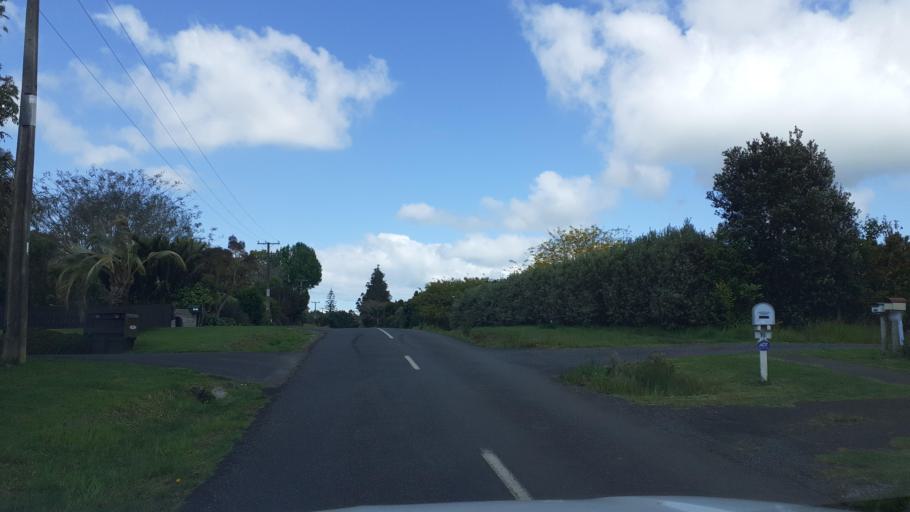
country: NZ
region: Northland
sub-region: Far North District
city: Kerikeri
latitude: -35.2403
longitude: 173.9587
